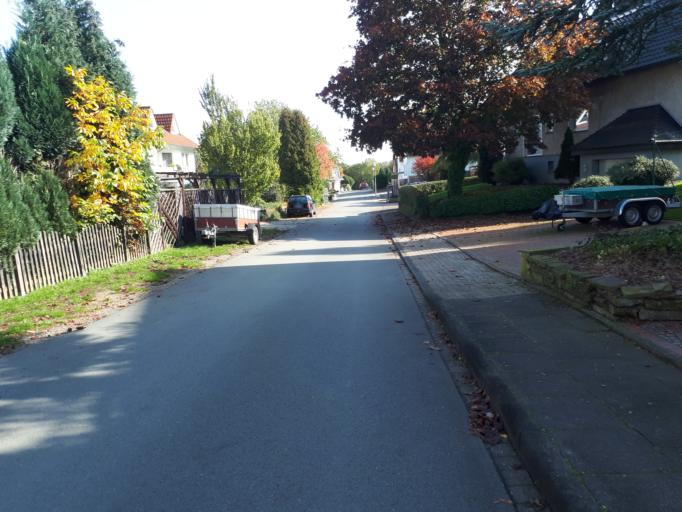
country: DE
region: North Rhine-Westphalia
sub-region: Regierungsbezirk Detmold
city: Huellhorst
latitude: 52.2718
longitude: 8.7061
